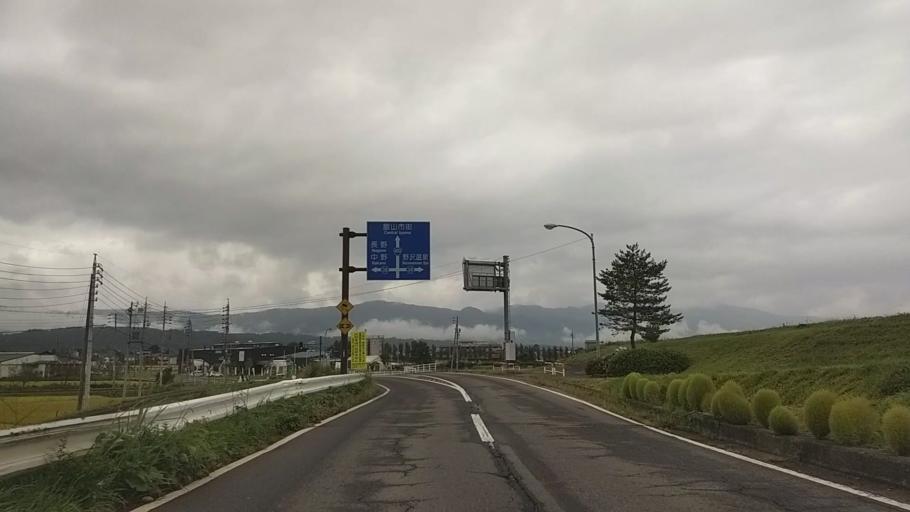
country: JP
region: Nagano
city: Iiyama
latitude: 36.8503
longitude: 138.3903
